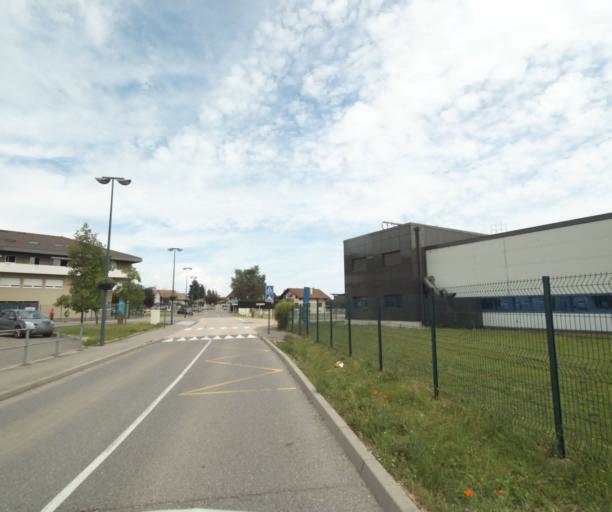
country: FR
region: Rhone-Alpes
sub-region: Departement de la Haute-Savoie
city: Anthy-sur-Leman
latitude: 46.3420
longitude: 6.4152
